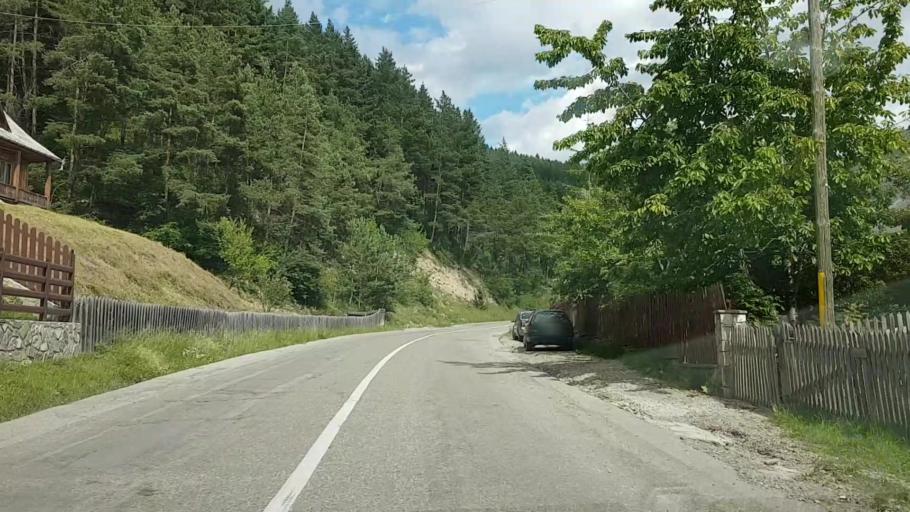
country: RO
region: Neamt
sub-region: Comuna Hangu
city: Hangu
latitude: 47.0100
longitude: 26.0862
